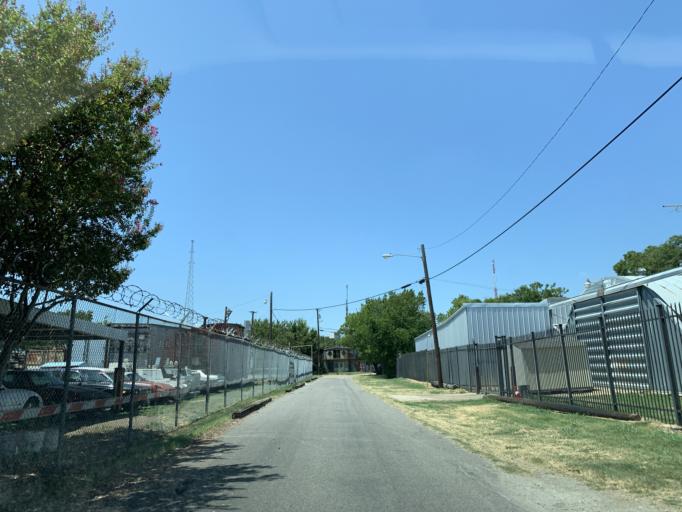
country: US
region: Texas
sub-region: Dallas County
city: Dallas
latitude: 32.7783
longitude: -96.7685
